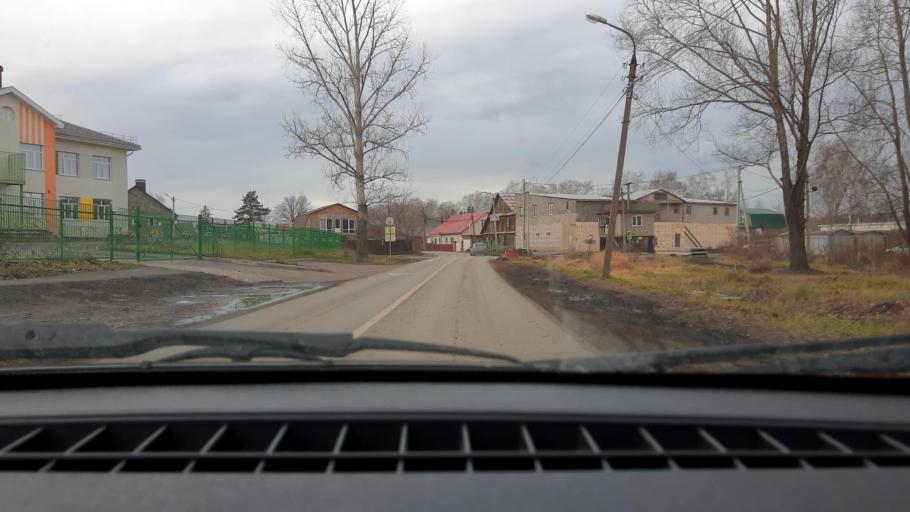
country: RU
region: Bashkortostan
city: Iglino
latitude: 54.8255
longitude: 56.1827
